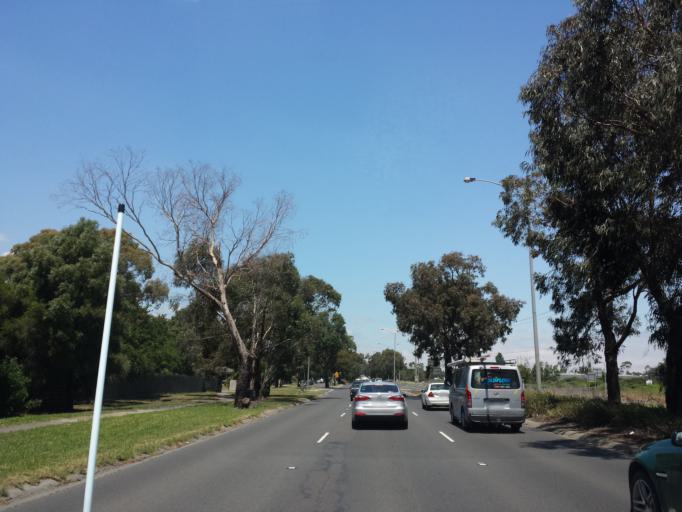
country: AU
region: Victoria
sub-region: Maroondah
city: Bayswater North
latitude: -37.8276
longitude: 145.2876
